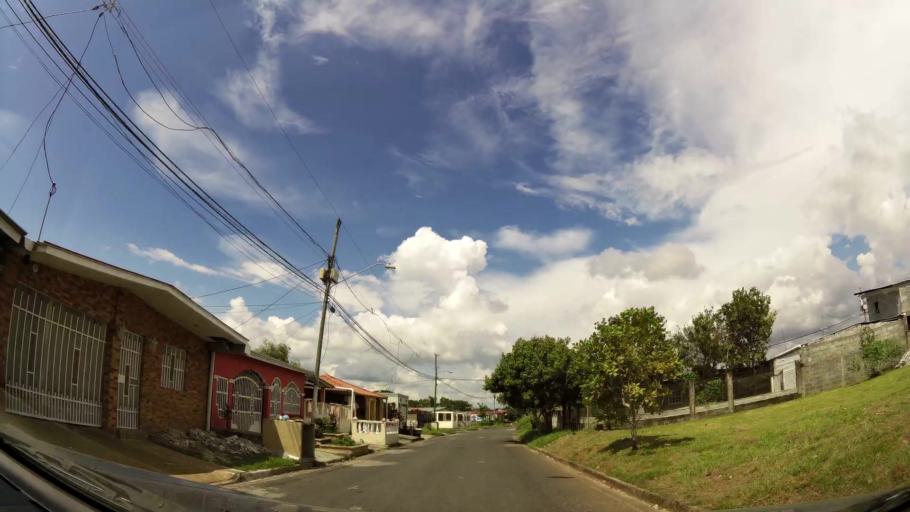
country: PA
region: Panama
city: Nuevo Arraijan
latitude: 8.9028
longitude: -79.7125
